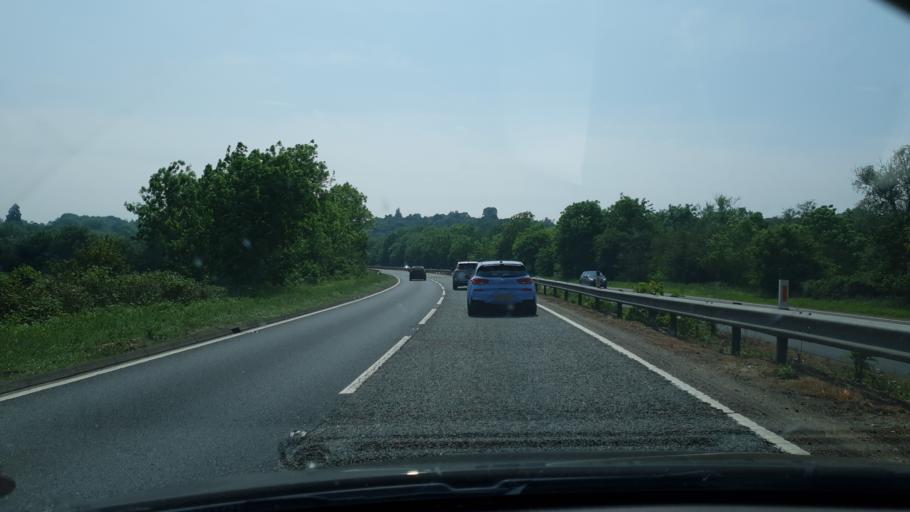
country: GB
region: England
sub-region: Suffolk
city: East Bergholt
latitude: 51.9652
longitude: 0.9734
